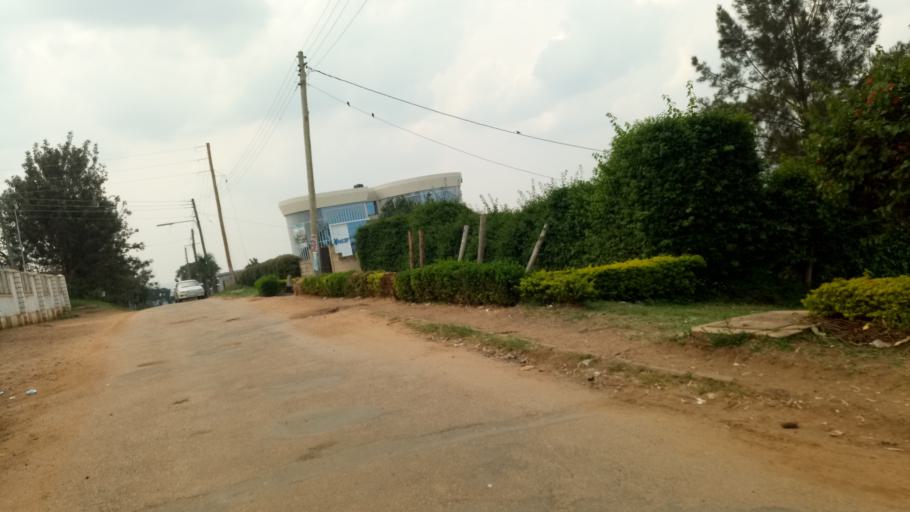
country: UG
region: Western Region
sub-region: Mbarara District
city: Mbarara
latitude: -0.6111
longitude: 30.6593
